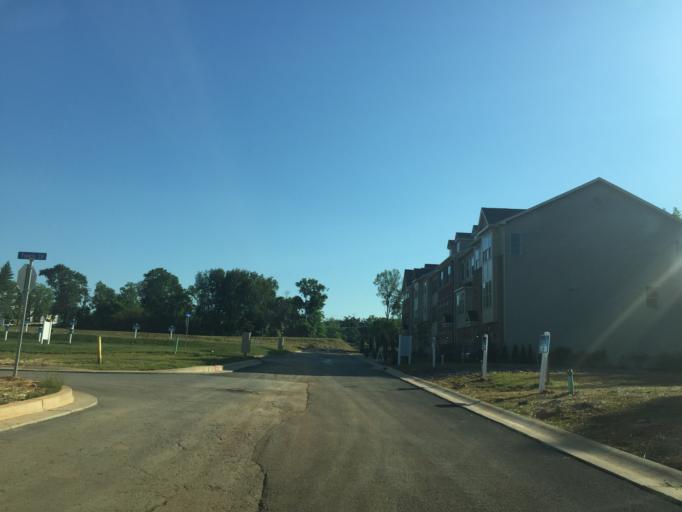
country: US
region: Maryland
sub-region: Anne Arundel County
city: Jessup
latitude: 39.1390
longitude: -76.7590
